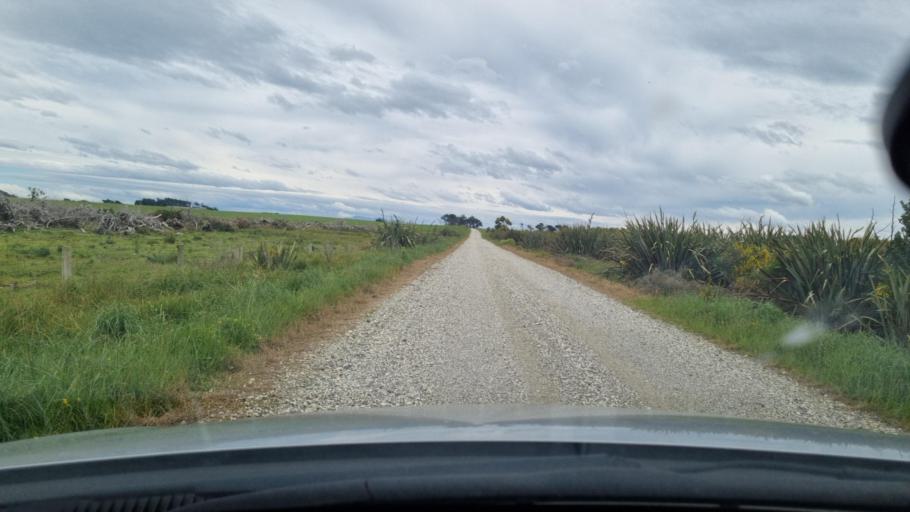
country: NZ
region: Southland
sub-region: Invercargill City
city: Invercargill
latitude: -46.3960
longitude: 168.2684
